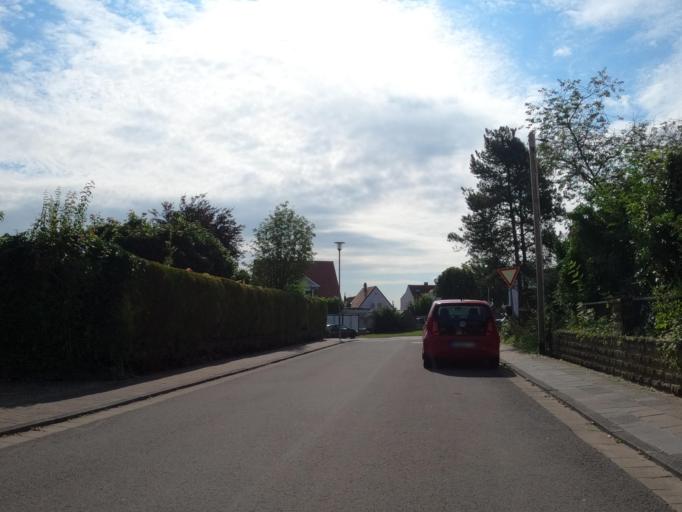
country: DE
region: Rheinland-Pfalz
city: Kirchheim an der Weinstrasse
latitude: 49.5357
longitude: 8.1790
